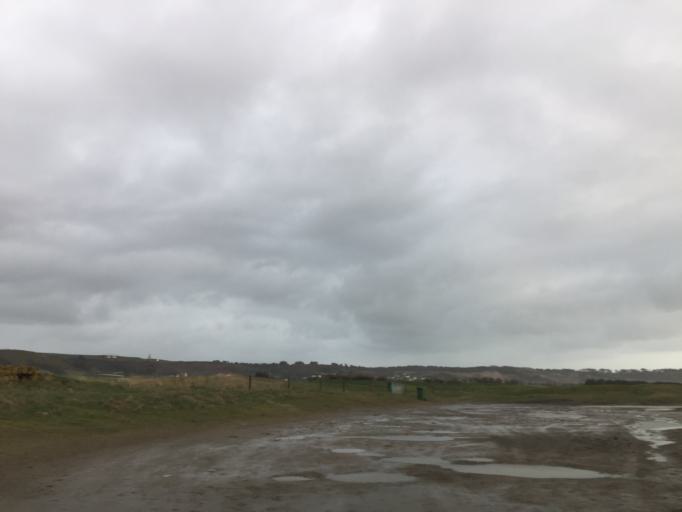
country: JE
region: St Helier
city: Saint Helier
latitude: 49.2120
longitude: -2.2240
